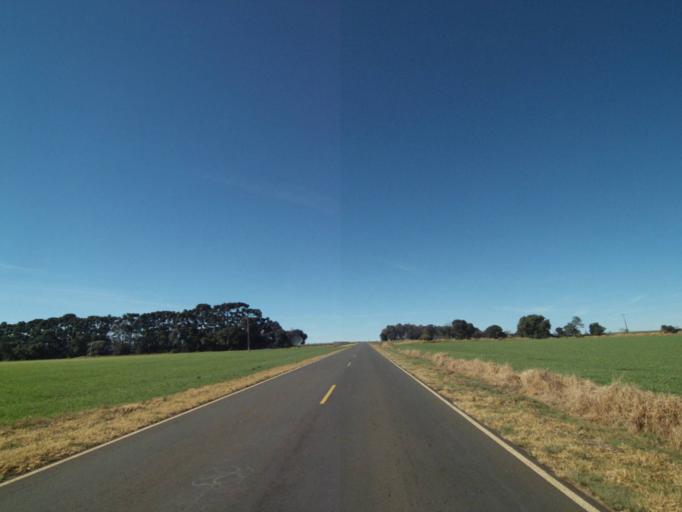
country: BR
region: Parana
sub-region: Tibagi
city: Tibagi
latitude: -24.5485
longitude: -50.2959
